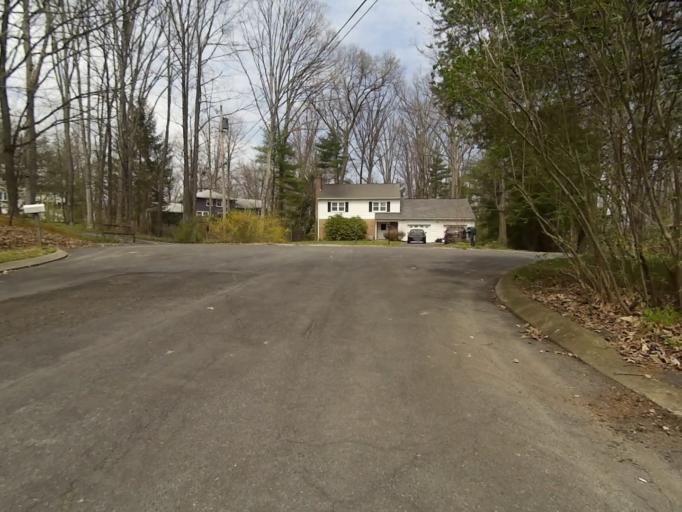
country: US
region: Pennsylvania
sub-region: Centre County
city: Park Forest Village
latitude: 40.8000
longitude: -77.9012
